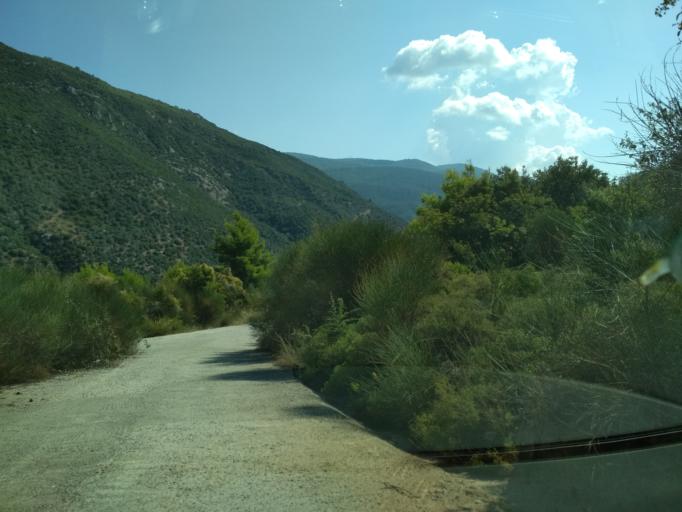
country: GR
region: Central Greece
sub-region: Nomos Evvoias
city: Oreoi
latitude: 38.8529
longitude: 23.1179
